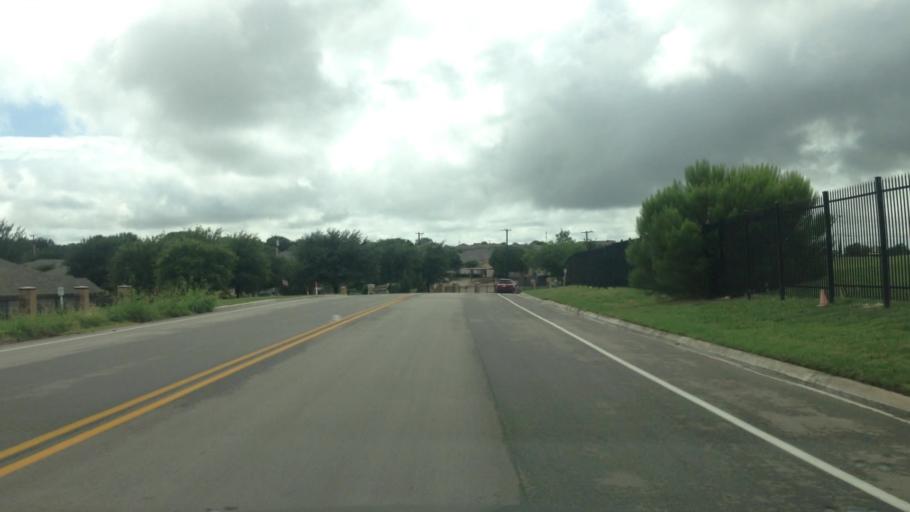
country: US
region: Texas
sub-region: Tarrant County
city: White Settlement
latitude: 32.7437
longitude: -97.4633
